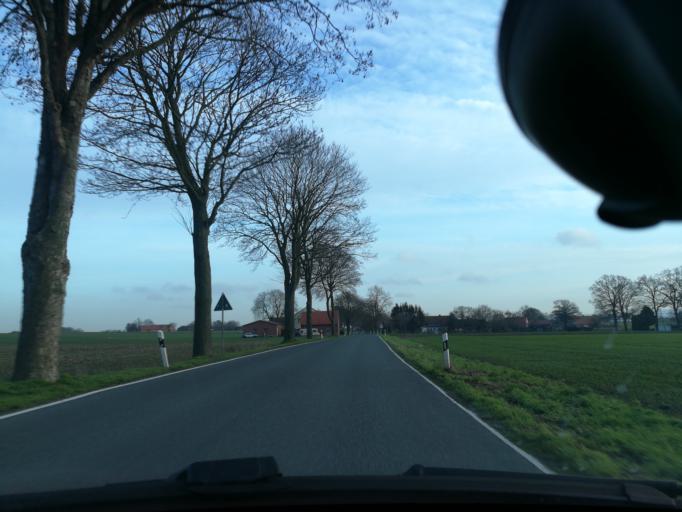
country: DE
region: North Rhine-Westphalia
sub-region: Regierungsbezirk Detmold
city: Hille
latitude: 52.3472
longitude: 8.7229
